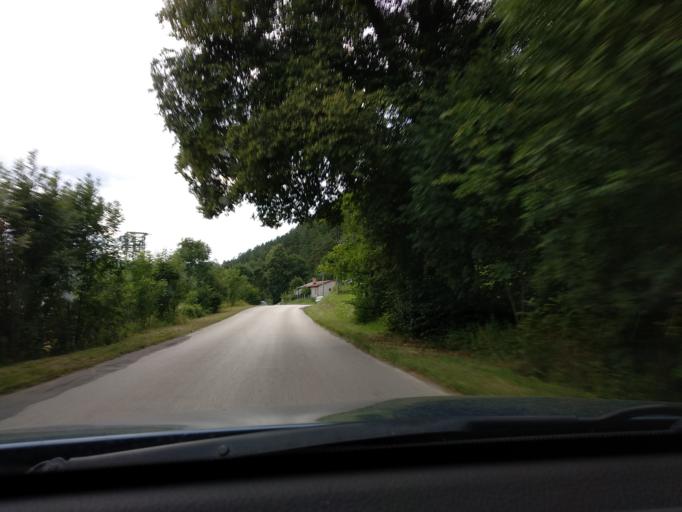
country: SK
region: Zilinsky
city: Ruzomberok
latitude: 49.0866
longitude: 19.3375
